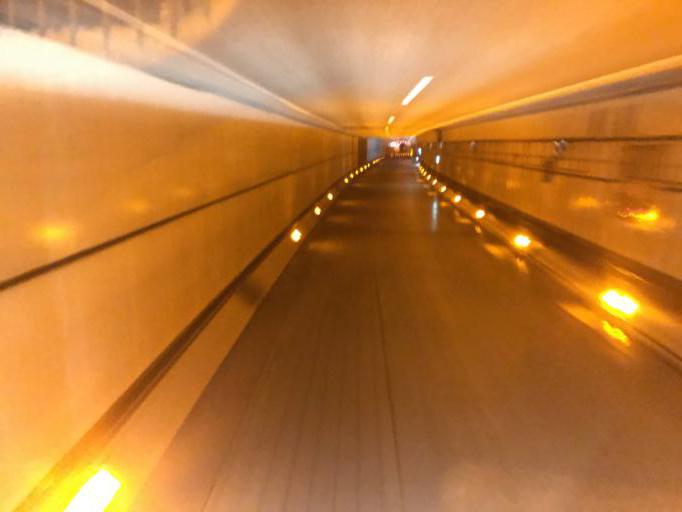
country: JP
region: Tokyo
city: Tokyo
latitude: 35.6881
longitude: 139.7086
